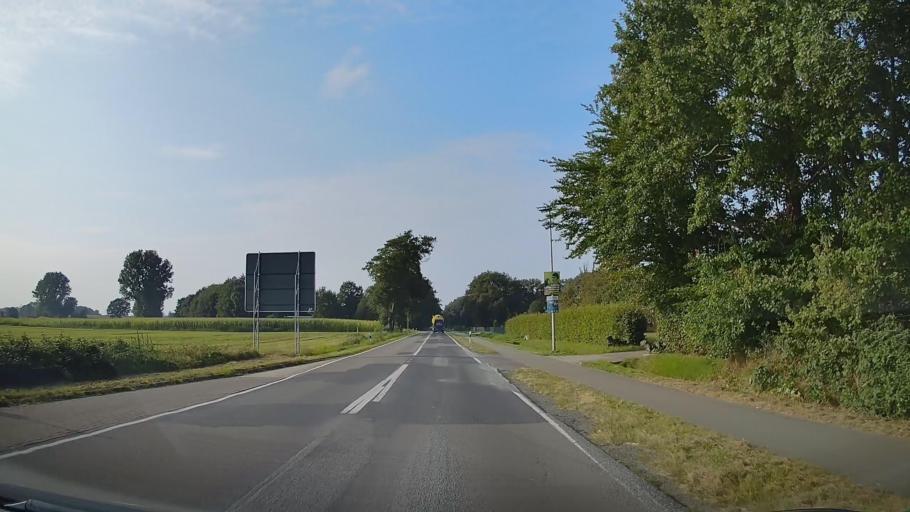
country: DE
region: Lower Saxony
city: Friesoythe
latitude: 53.1103
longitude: 7.8296
